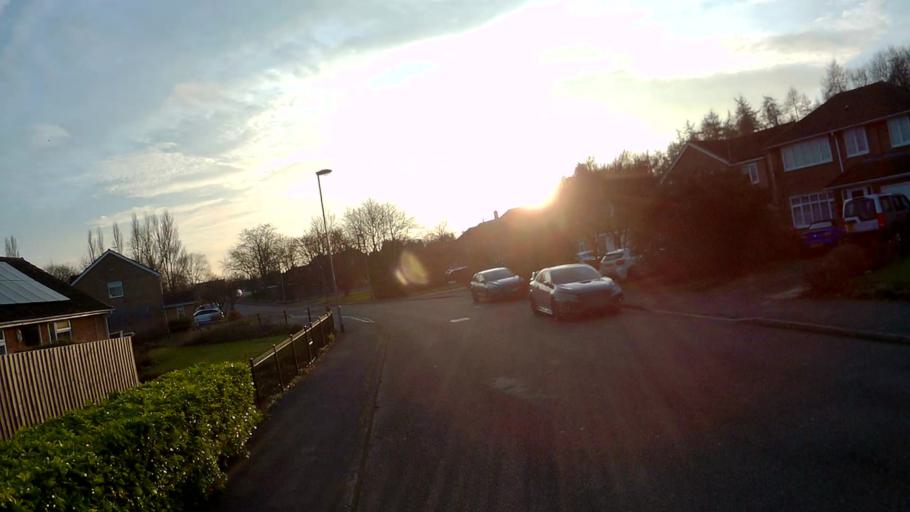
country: GB
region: England
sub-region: Lincolnshire
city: Bourne
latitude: 52.7720
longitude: -0.3919
